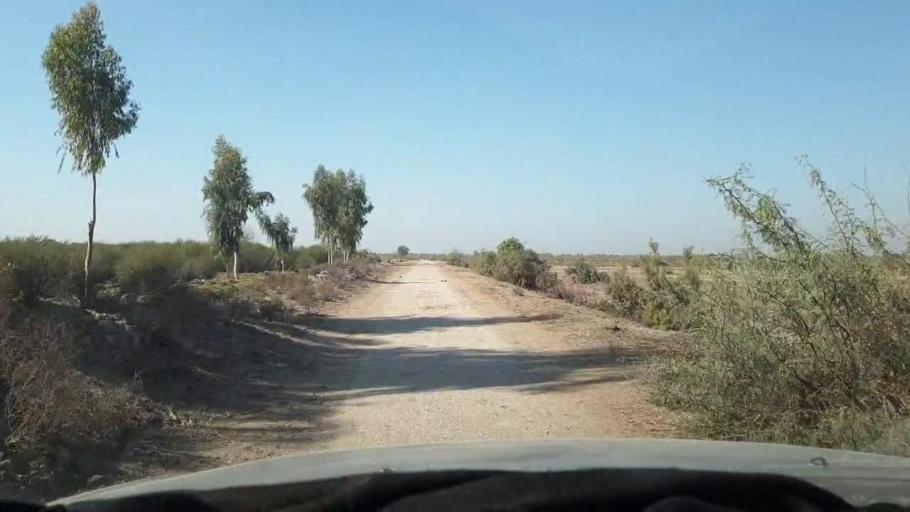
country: PK
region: Sindh
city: Adilpur
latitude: 27.8951
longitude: 69.2502
